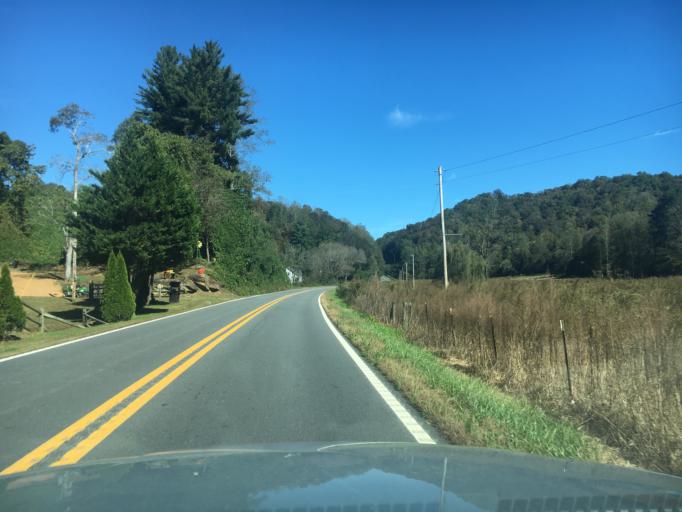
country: US
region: North Carolina
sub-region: Burke County
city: Glen Alpine
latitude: 35.5565
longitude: -81.8545
